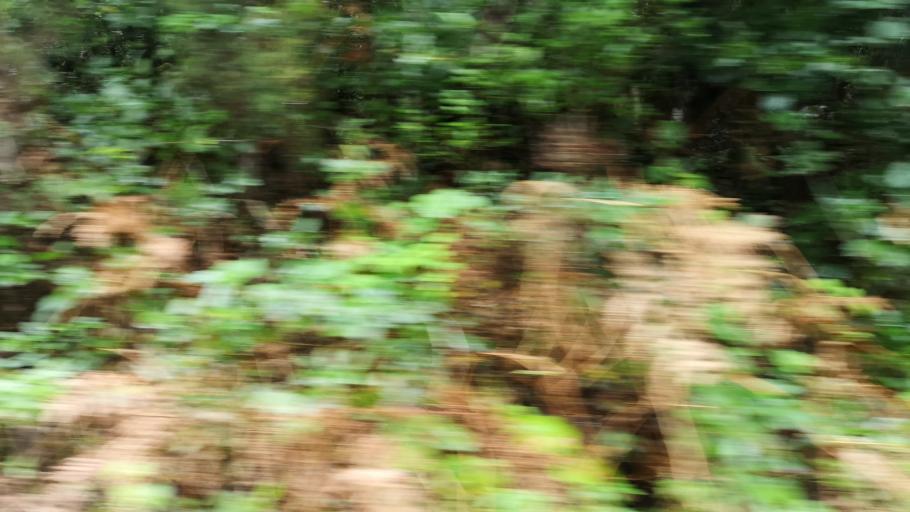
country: ES
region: Canary Islands
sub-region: Provincia de Santa Cruz de Tenerife
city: Vallehermosa
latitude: 28.1629
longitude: -17.2951
